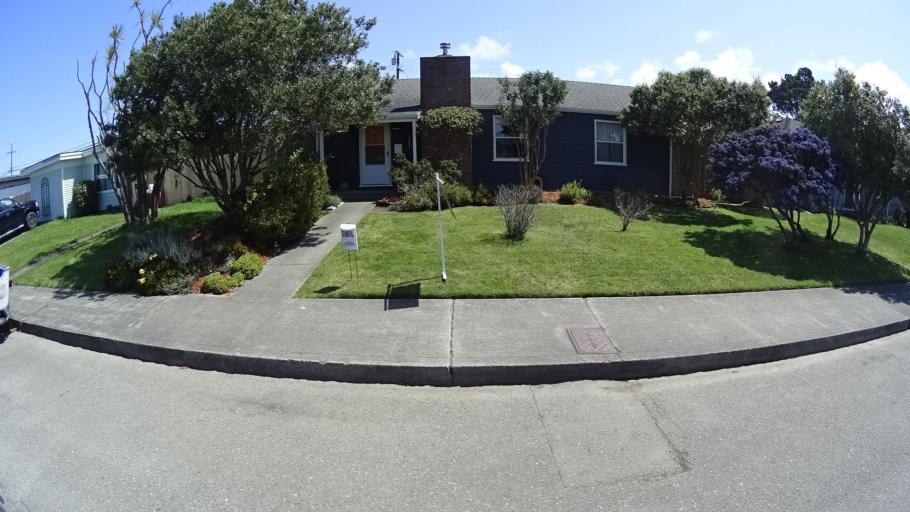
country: US
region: California
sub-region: Humboldt County
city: Bayview
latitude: 40.7774
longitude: -124.1835
